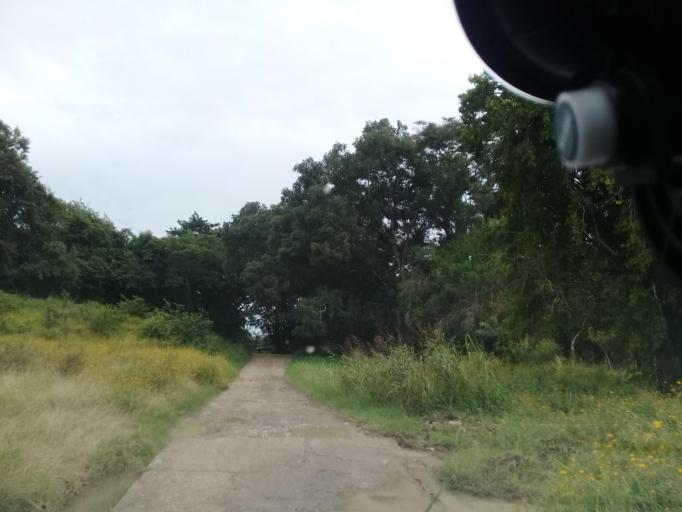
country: MX
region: Hidalgo
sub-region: Huejutla de Reyes
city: Chalahuiyapa
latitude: 21.1700
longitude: -98.3720
